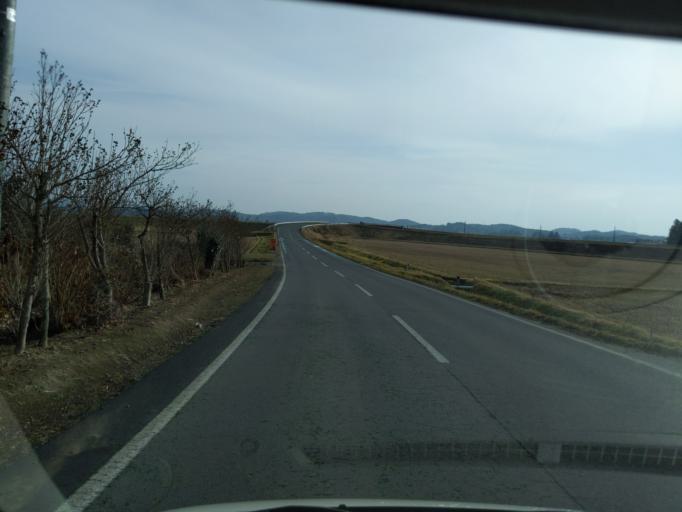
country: JP
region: Iwate
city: Ichinoseki
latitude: 38.7829
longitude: 141.1743
